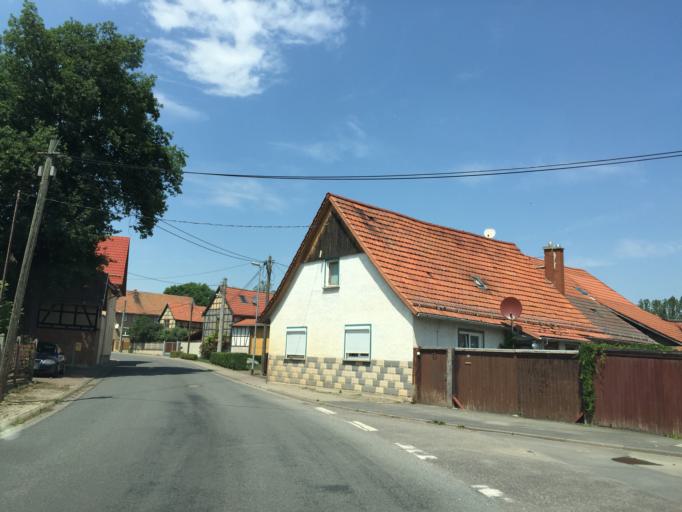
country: DE
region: Thuringia
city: Witzleben
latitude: 50.8172
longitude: 11.1382
